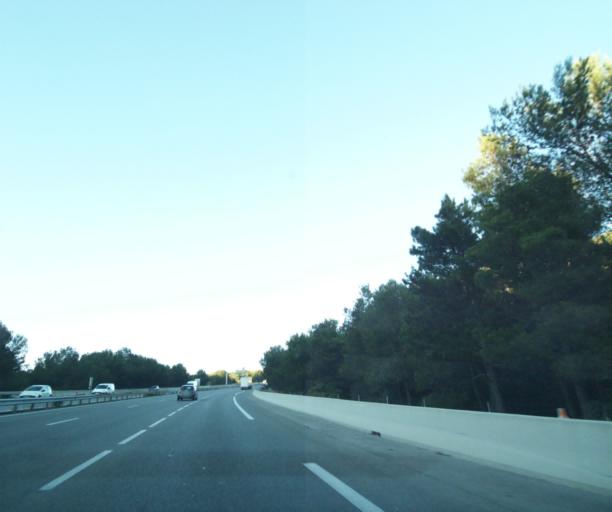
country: FR
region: Provence-Alpes-Cote d'Azur
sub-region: Departement des Bouches-du-Rhone
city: Roquefort-la-Bedoule
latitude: 43.2199
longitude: 5.5812
